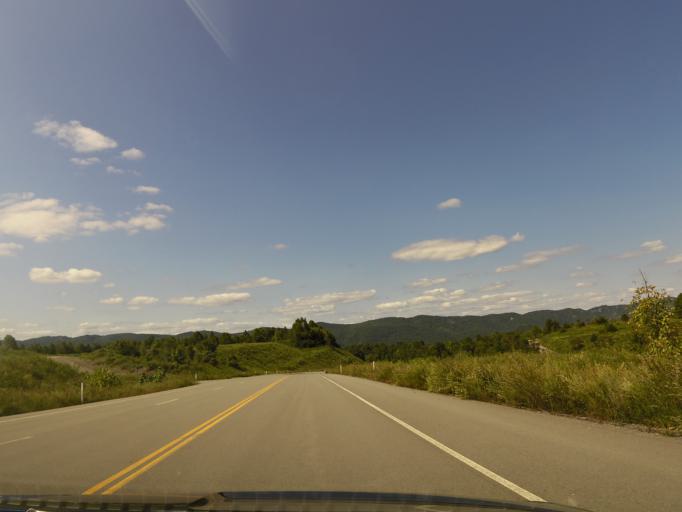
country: US
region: Kentucky
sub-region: Bell County
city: Pineville
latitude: 36.7317
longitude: -83.5892
